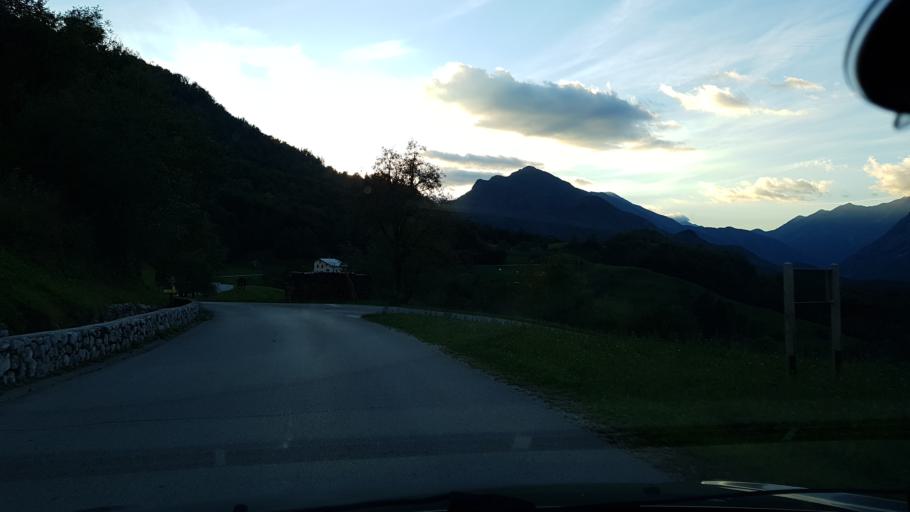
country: SI
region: Kobarid
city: Kobarid
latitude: 46.2562
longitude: 13.6118
